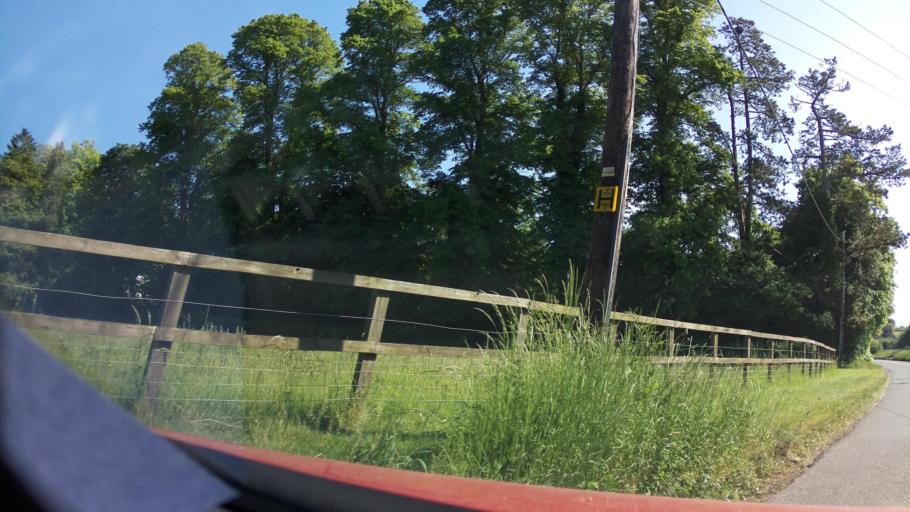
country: GB
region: England
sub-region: Hampshire
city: Abbotts Ann
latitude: 51.2308
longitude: -1.5643
